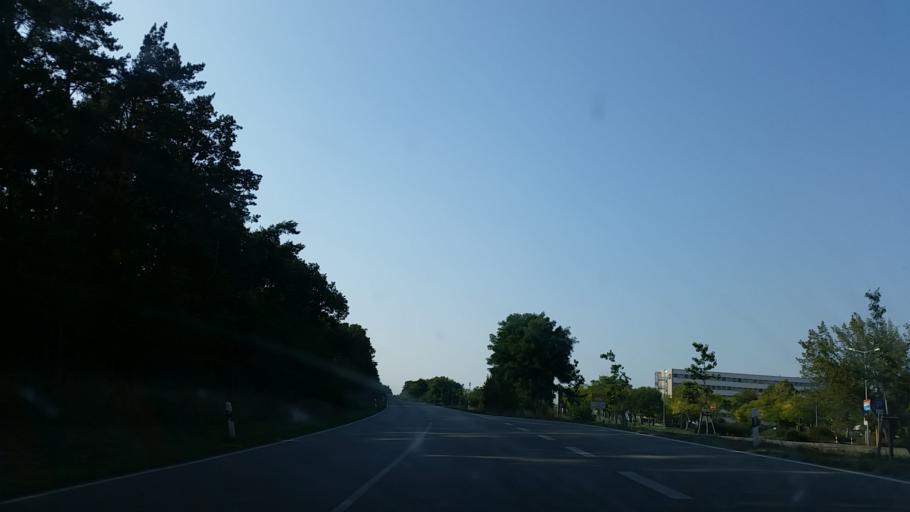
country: DE
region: Brandenburg
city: Meyenburg
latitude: 53.0867
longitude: 14.2275
